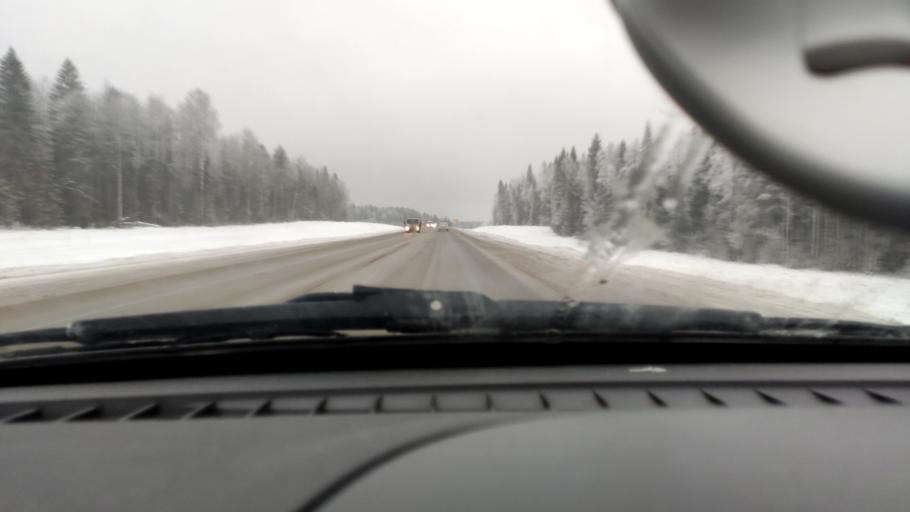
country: RU
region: Perm
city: Polazna
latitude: 58.1212
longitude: 56.4244
